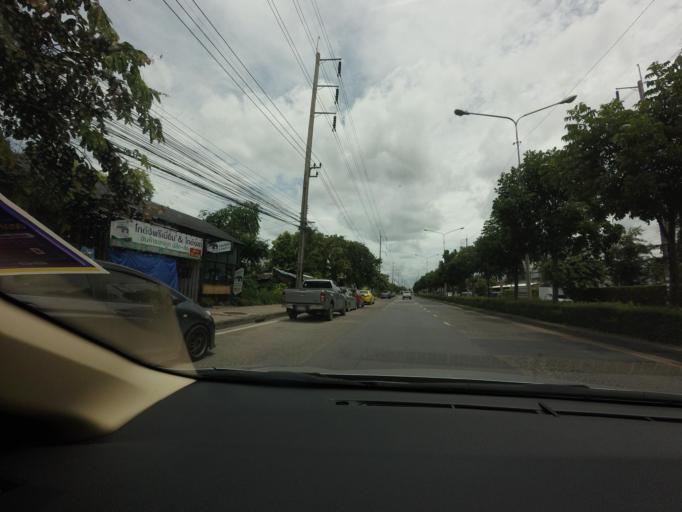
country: TH
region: Bangkok
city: Lat Krabang
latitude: 13.7167
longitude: 100.8046
